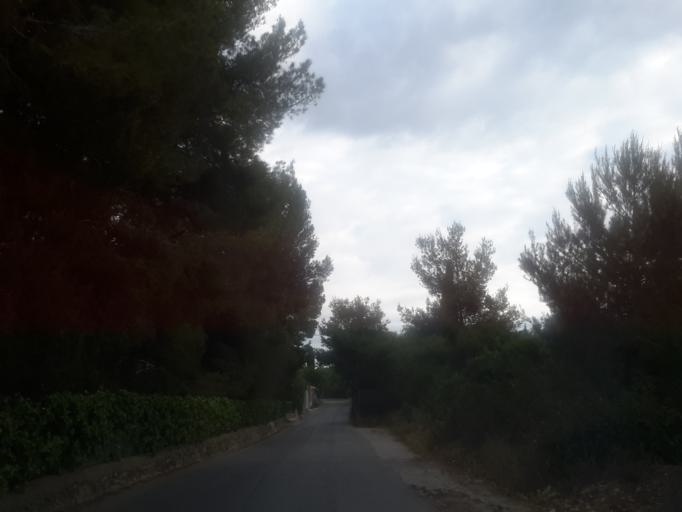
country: ES
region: Catalonia
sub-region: Provincia de Barcelona
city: Cubelles
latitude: 41.2302
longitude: 1.6913
